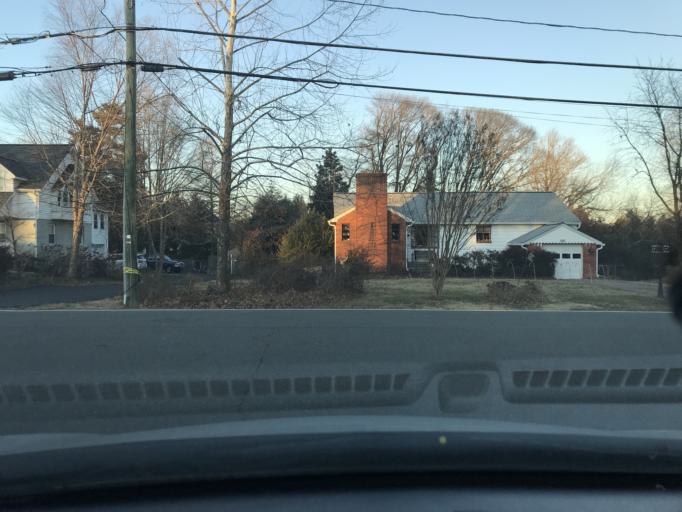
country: US
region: Virginia
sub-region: City of Fairfax
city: Fairfax
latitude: 38.8629
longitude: -77.3095
